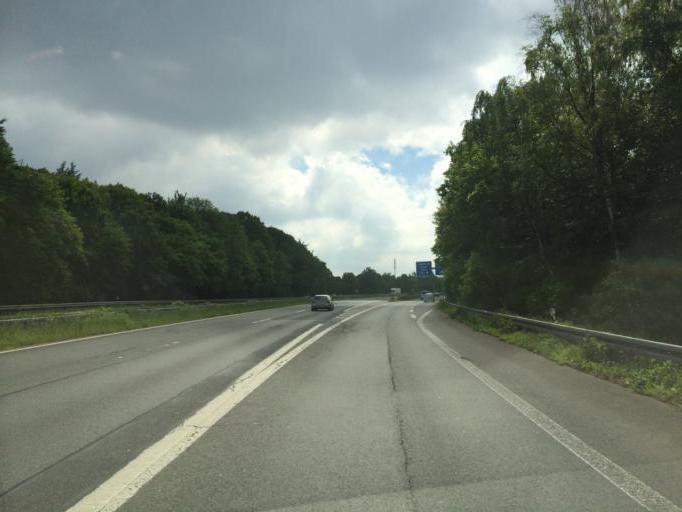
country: DE
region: North Rhine-Westphalia
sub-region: Regierungsbezirk Arnsberg
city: Dortmund
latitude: 51.4484
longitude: 7.4863
